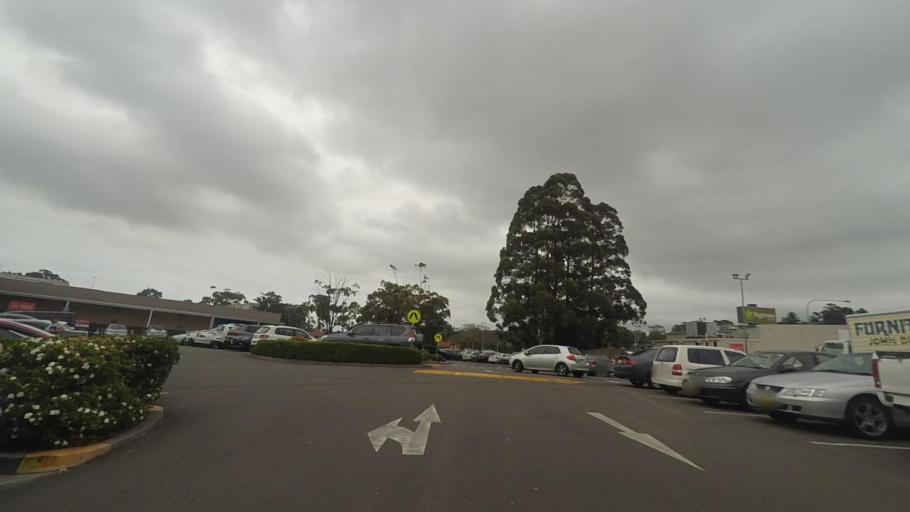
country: AU
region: New South Wales
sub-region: Wollongong
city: Mangerton
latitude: -34.4353
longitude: 150.8627
